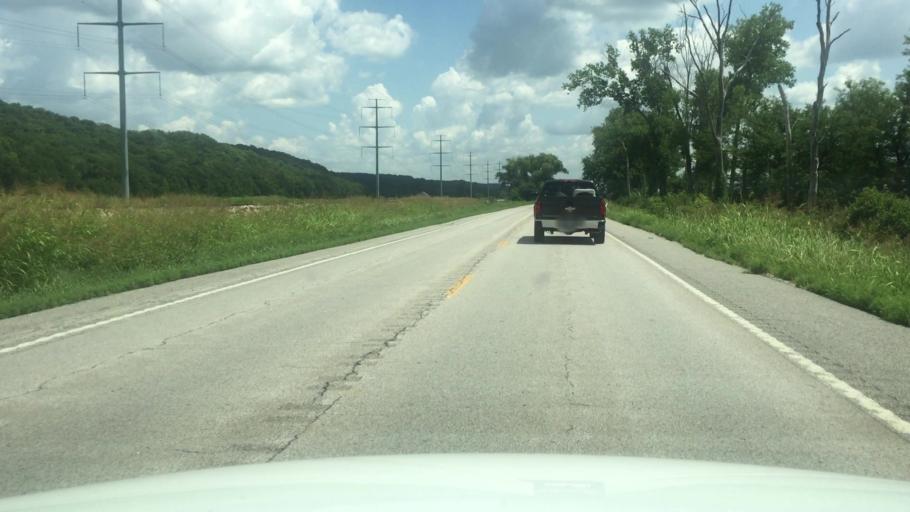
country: US
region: Missouri
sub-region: Platte County
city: Weston
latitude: 39.4460
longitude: -94.9515
